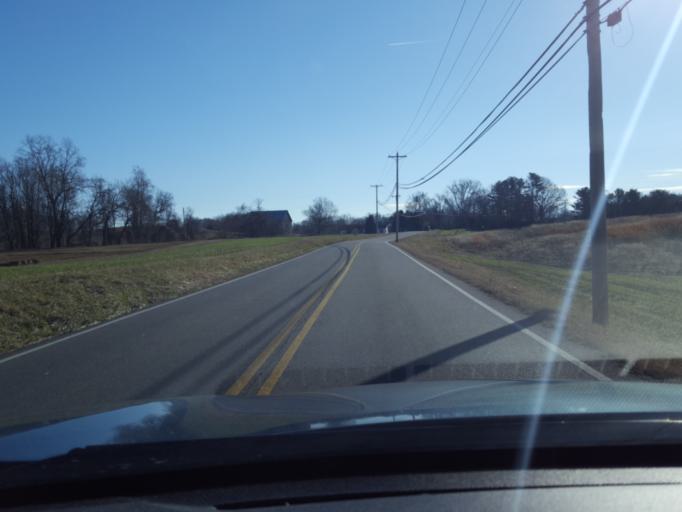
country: US
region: Maryland
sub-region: Calvert County
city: Huntingtown Town Center
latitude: 38.6649
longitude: -76.5944
